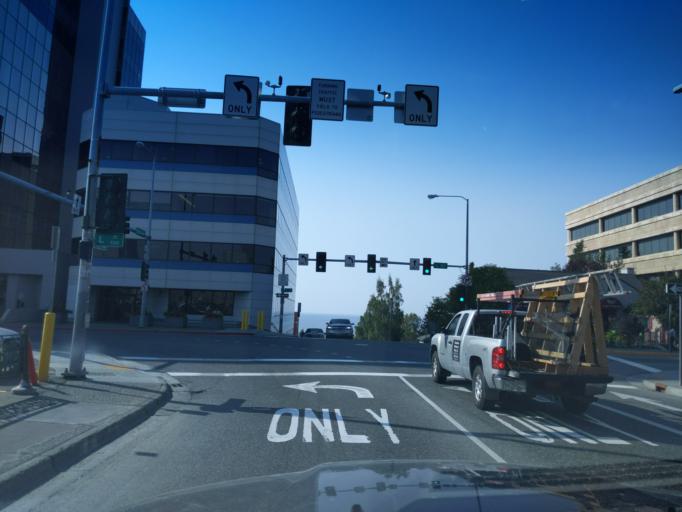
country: US
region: Alaska
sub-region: Anchorage Municipality
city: Anchorage
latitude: 61.2176
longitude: -149.9033
